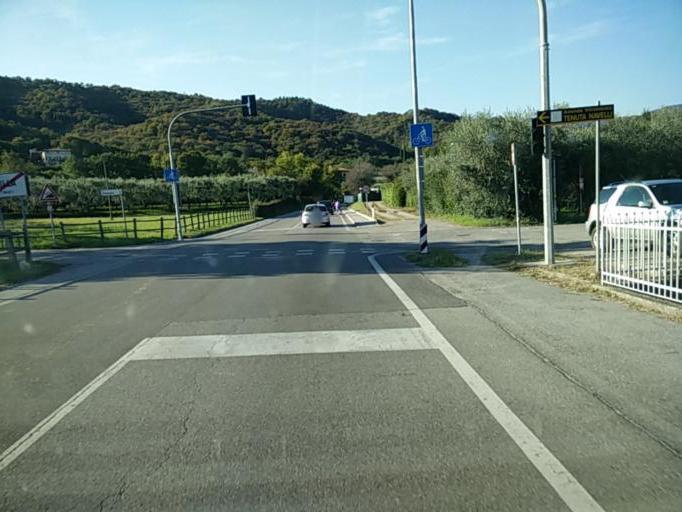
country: IT
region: Lombardy
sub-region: Provincia di Brescia
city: Cunettone-Villa
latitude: 45.5923
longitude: 10.5065
